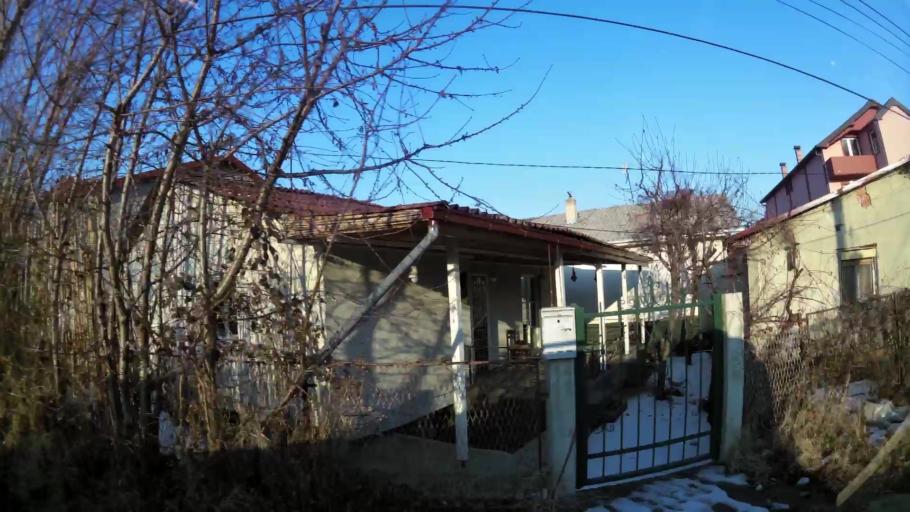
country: MK
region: Kisela Voda
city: Usje
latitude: 41.9710
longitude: 21.4710
